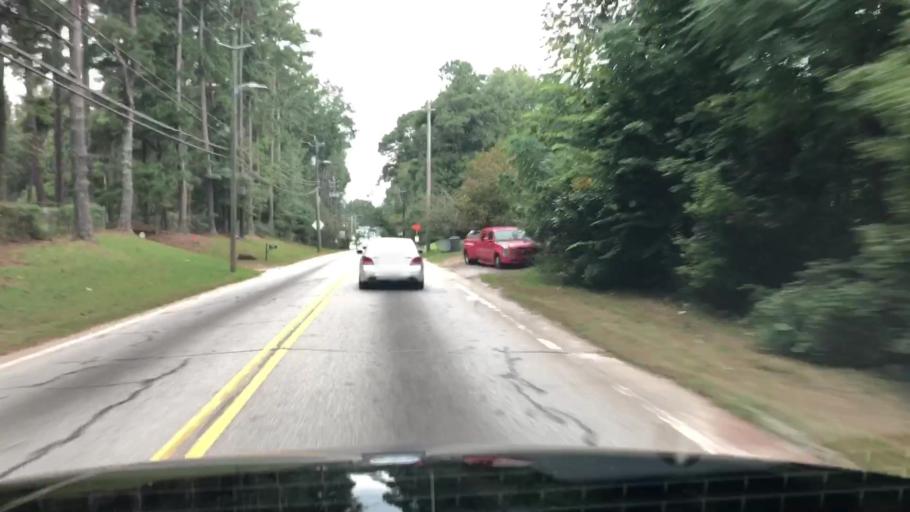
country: US
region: Georgia
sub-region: Fulton County
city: College Park
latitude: 33.6958
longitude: -84.5307
